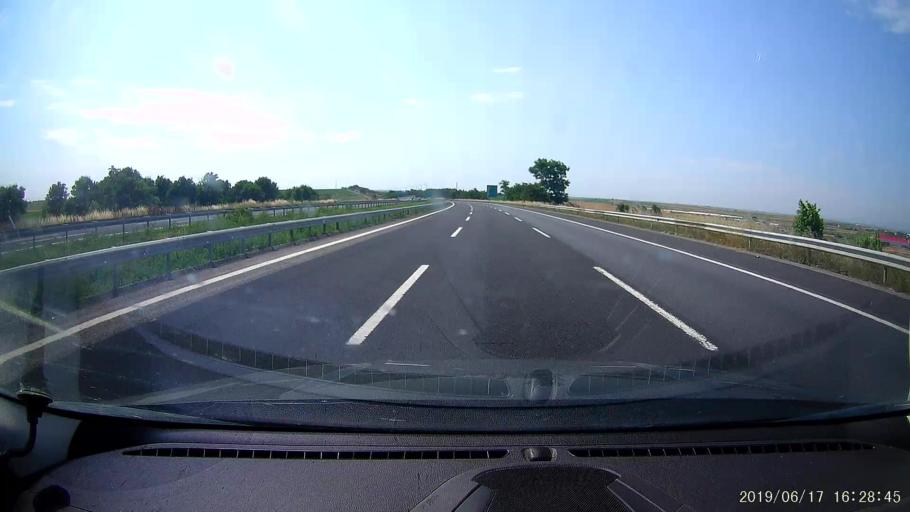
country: TR
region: Tekirdag
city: Beyazkoy
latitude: 41.3290
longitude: 27.7014
